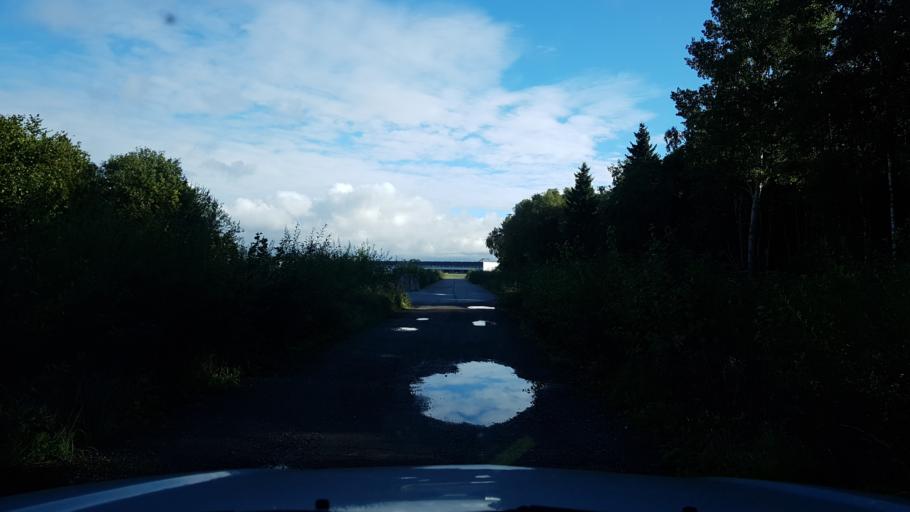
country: EE
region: Harju
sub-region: Rae vald
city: Jueri
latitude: 59.3402
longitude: 24.8959
